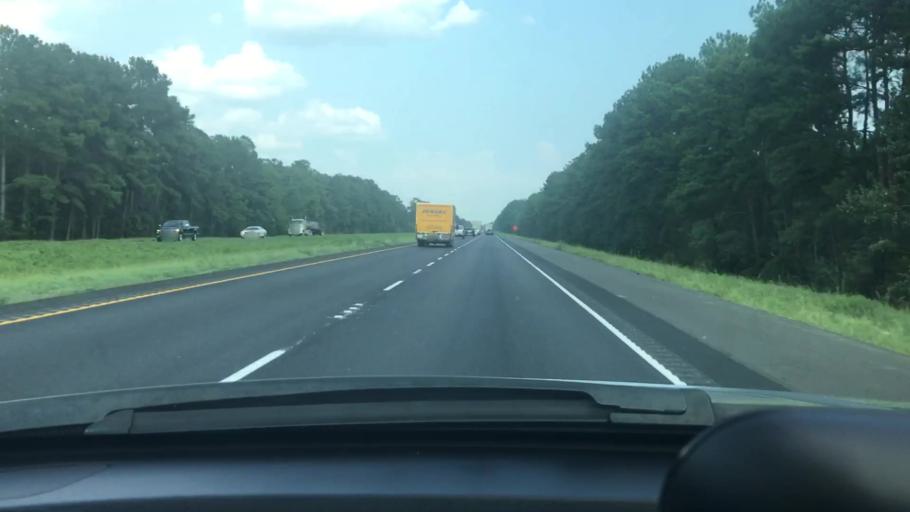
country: US
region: Louisiana
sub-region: Livingston Parish
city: Livingston
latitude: 30.4752
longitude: -90.6903
